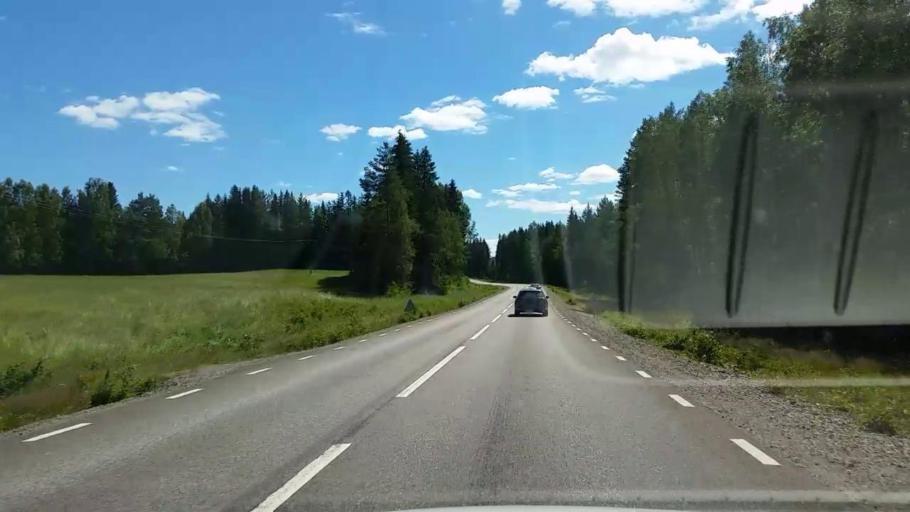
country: SE
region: Gaevleborg
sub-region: Ovanakers Kommun
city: Edsbyn
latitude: 61.1973
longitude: 15.8738
